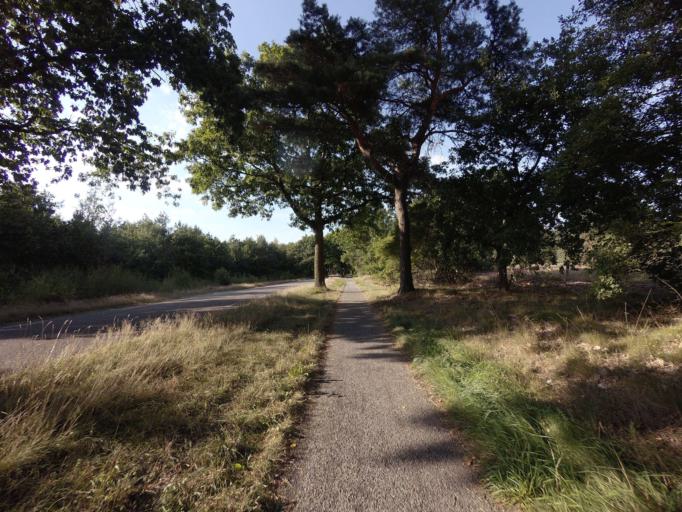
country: NL
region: North Brabant
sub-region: Gemeente Heeze-Leende
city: Heeze
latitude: 51.3761
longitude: 5.6248
